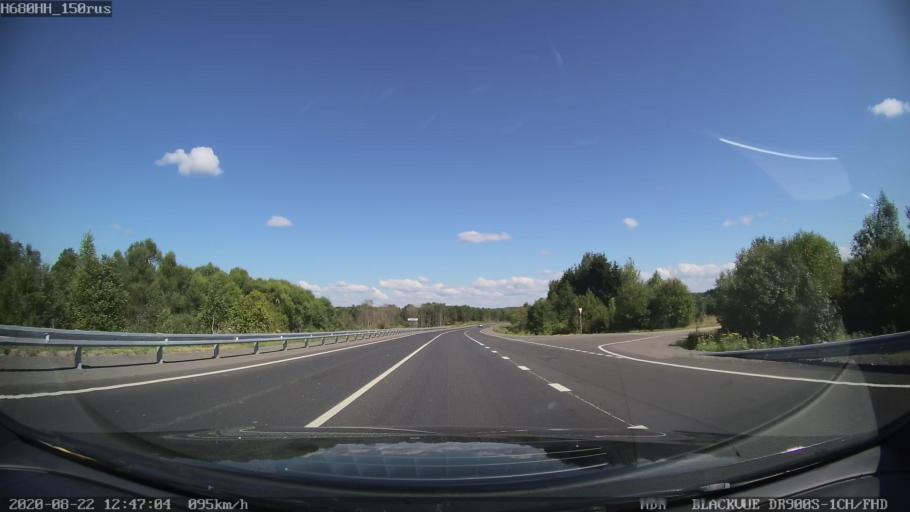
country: RU
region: Tverskaya
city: Rameshki
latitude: 57.4266
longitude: 36.1578
